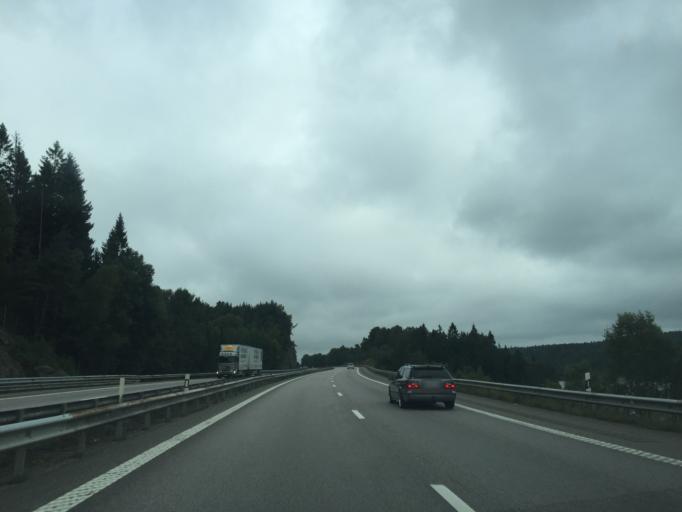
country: SE
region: Halland
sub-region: Kungsbacka Kommun
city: Fjaeras kyrkby
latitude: 57.3912
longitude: 12.1890
